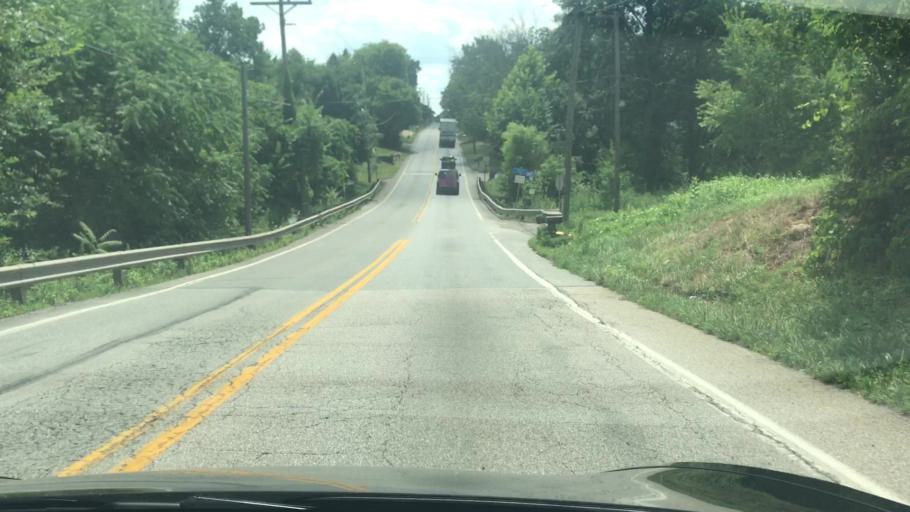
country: US
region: Pennsylvania
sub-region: York County
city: Manchester
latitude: 40.0756
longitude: -76.7655
